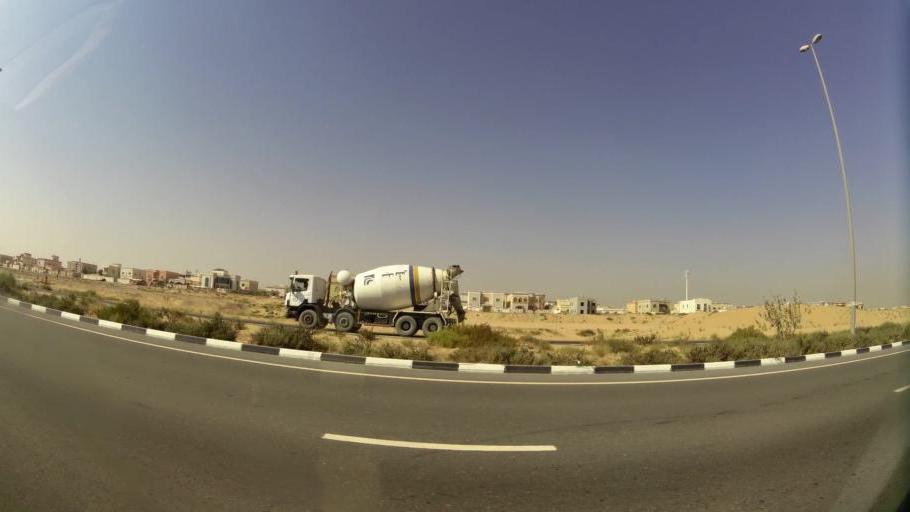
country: AE
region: Ajman
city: Ajman
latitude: 25.4167
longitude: 55.5477
